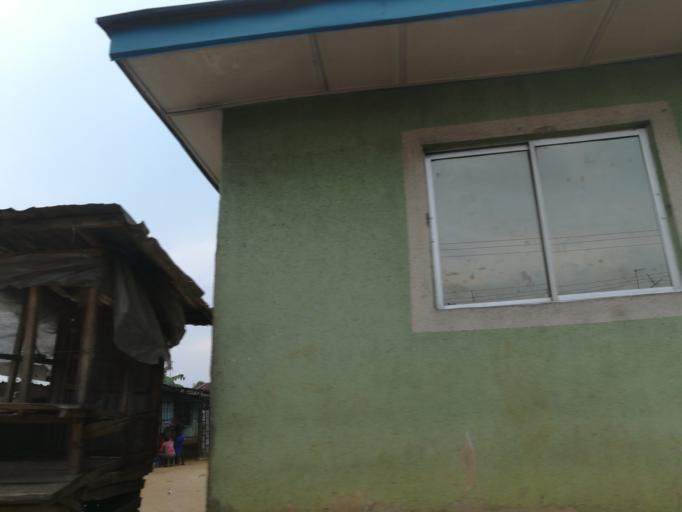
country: NG
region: Rivers
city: Okrika
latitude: 4.7834
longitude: 7.1281
